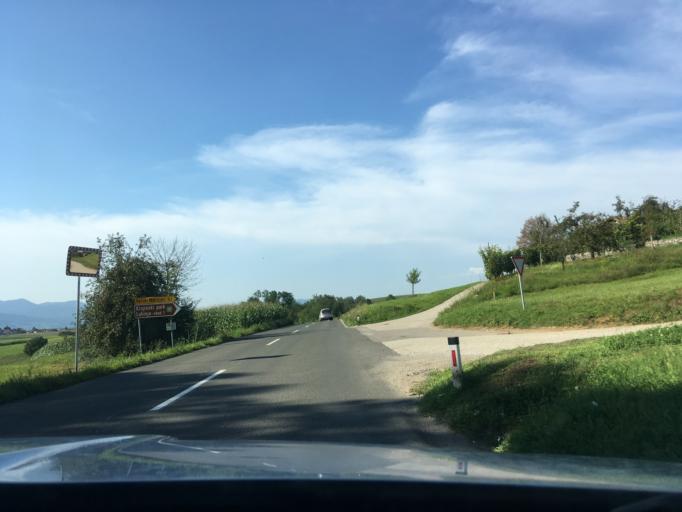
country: SI
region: Crnomelj
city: Crnomelj
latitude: 45.5095
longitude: 15.1862
